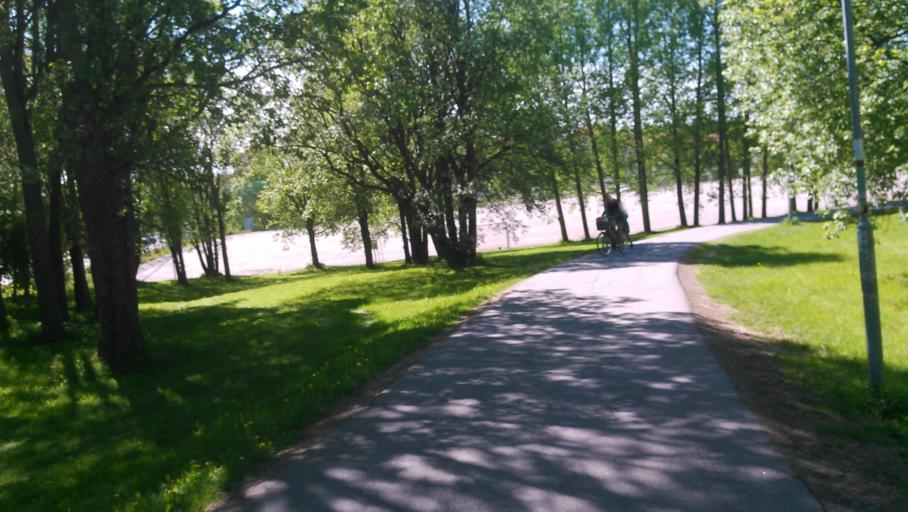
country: SE
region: Vaesterbotten
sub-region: Umea Kommun
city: Umea
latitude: 63.8231
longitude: 20.2957
